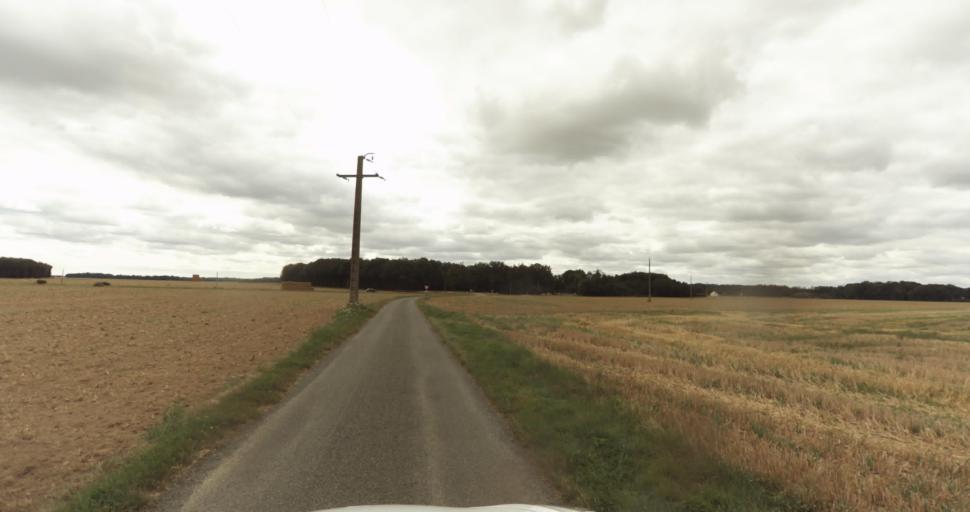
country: FR
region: Haute-Normandie
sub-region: Departement de l'Eure
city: La Madeleine-de-Nonancourt
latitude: 48.8169
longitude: 1.2163
